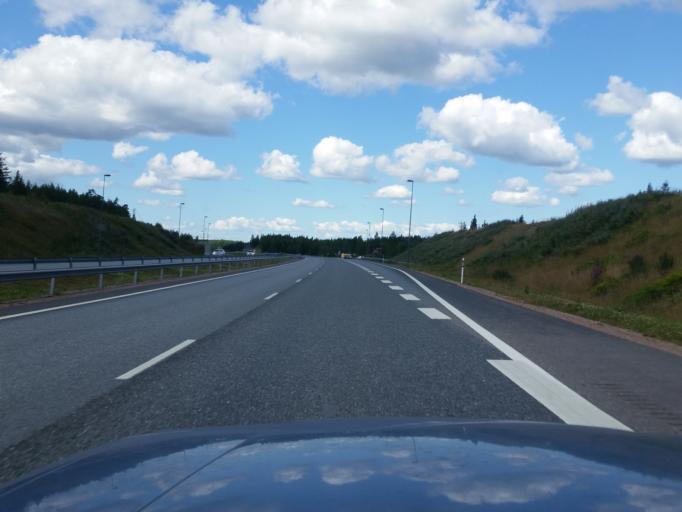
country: FI
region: Uusimaa
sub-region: Helsinki
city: Sammatti
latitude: 60.3675
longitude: 23.8696
